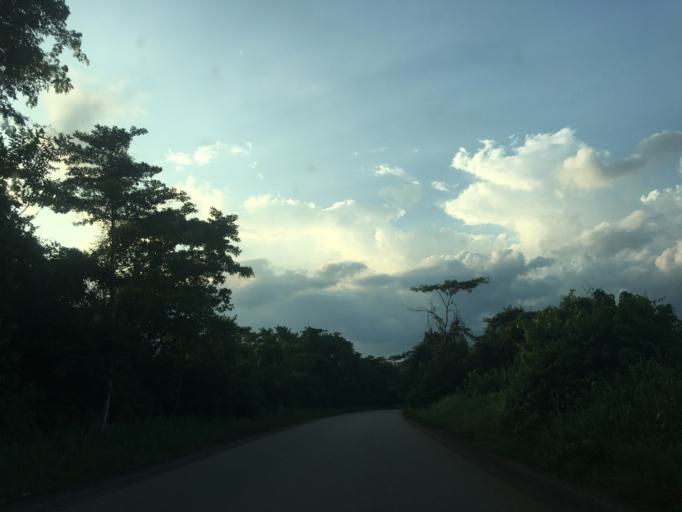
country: GH
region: Western
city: Bibiani
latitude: 6.6688
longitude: -2.4327
